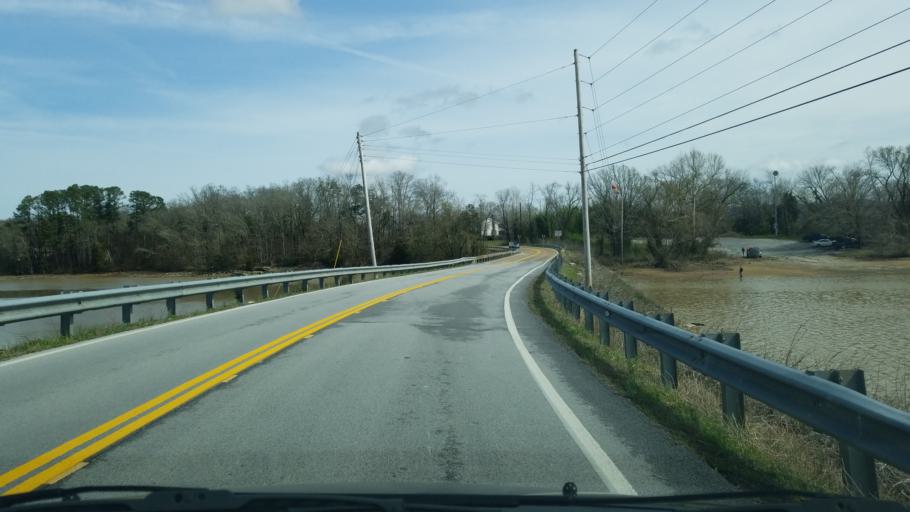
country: US
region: Tennessee
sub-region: Hamilton County
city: Lakesite
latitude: 35.1568
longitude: -85.0614
